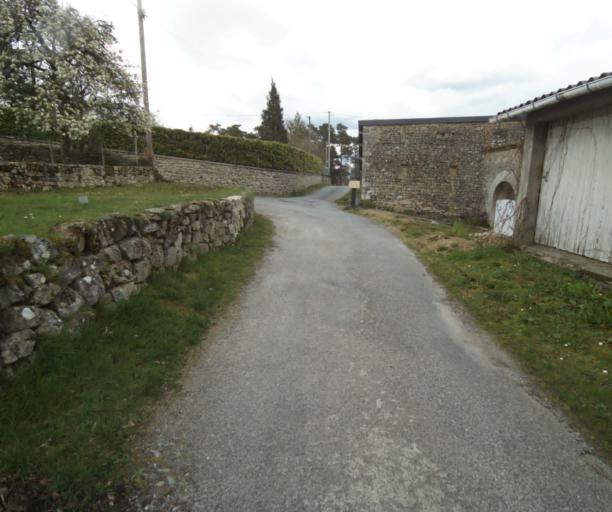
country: FR
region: Limousin
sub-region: Departement de la Correze
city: Correze
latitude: 45.2774
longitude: 1.9450
